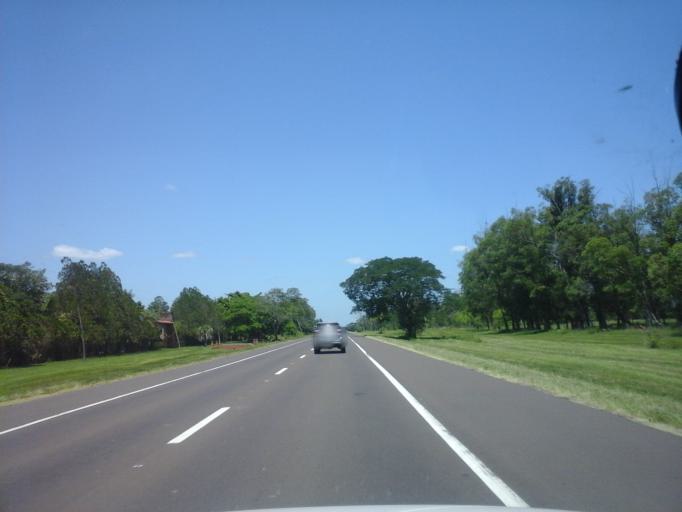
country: AR
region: Corrientes
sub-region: Departamento de San Cosme
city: San Cosme
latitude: -27.3638
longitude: -58.4453
